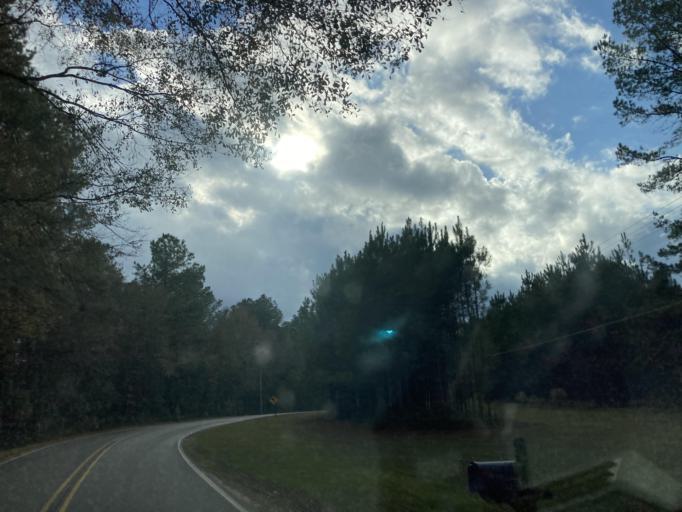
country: US
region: Mississippi
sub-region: Lamar County
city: Purvis
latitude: 31.1666
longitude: -89.5867
